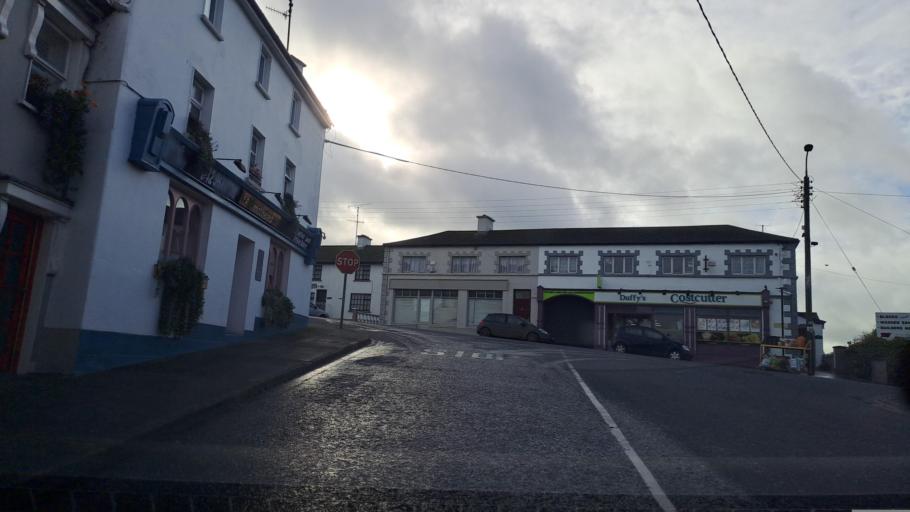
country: IE
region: Ulster
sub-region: An Cabhan
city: Bailieborough
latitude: 53.9958
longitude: -6.8988
